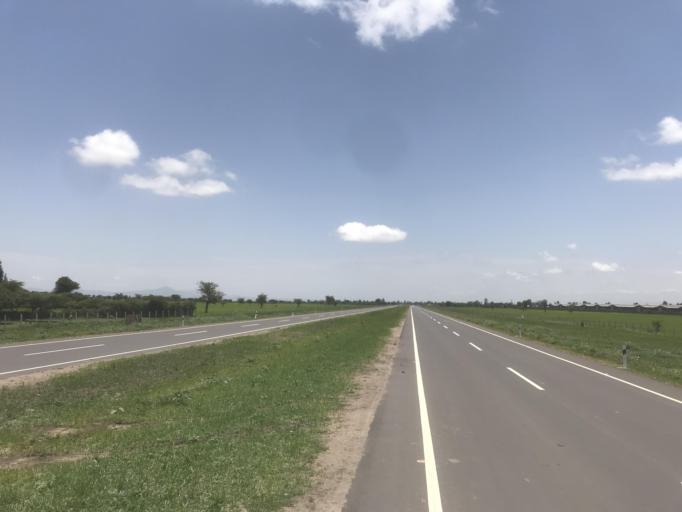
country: ET
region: Oromiya
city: Mojo
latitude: 8.5653
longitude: 39.1196
